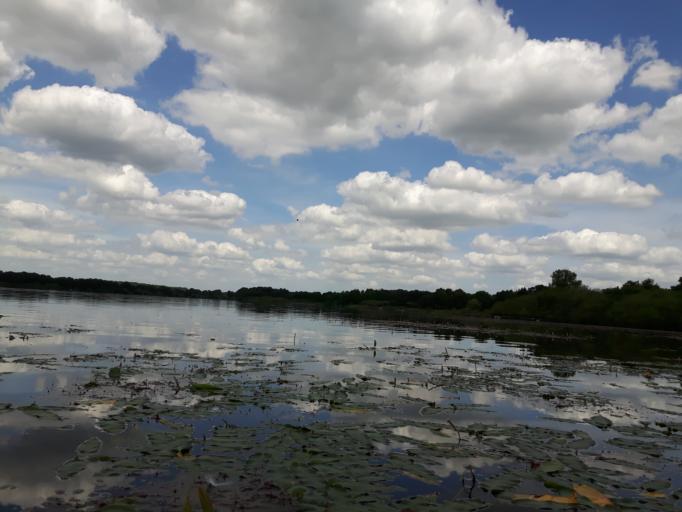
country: DE
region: Schleswig-Holstein
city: Muhbrook
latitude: 54.1421
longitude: 10.0081
